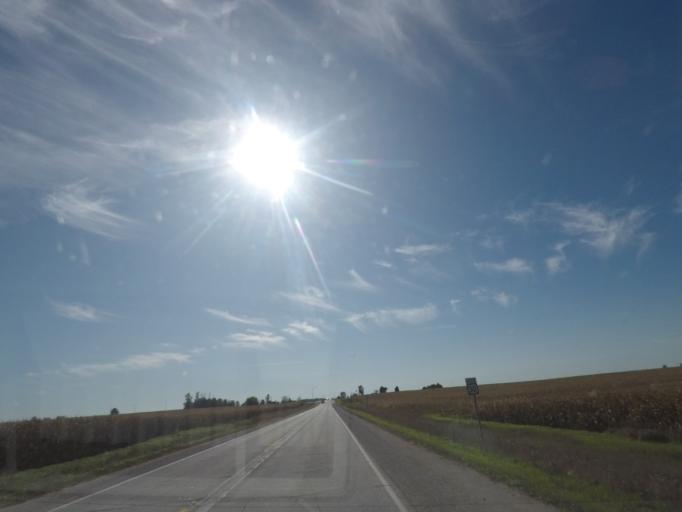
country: US
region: Iowa
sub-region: Story County
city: Nevada
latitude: 42.0121
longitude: -93.3094
